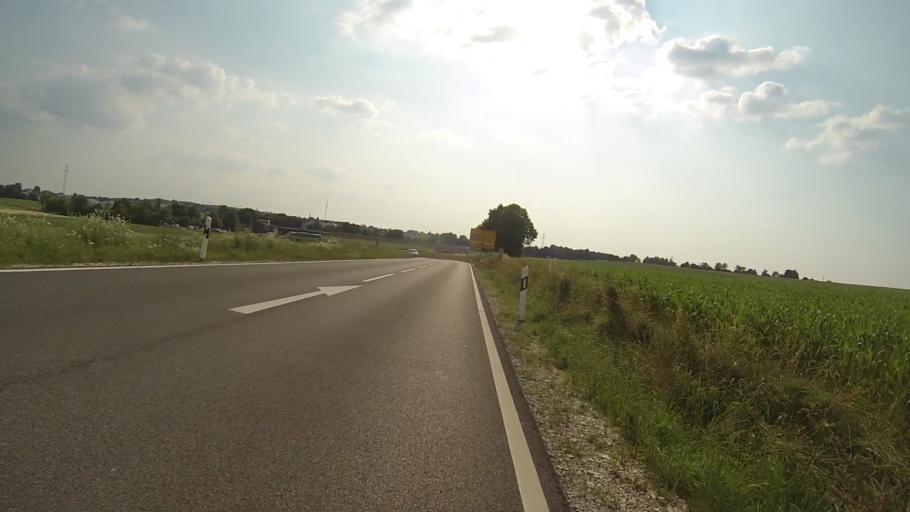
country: DE
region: Baden-Wuerttemberg
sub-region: Tuebingen Region
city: Ulm
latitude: 48.4398
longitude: 9.9788
